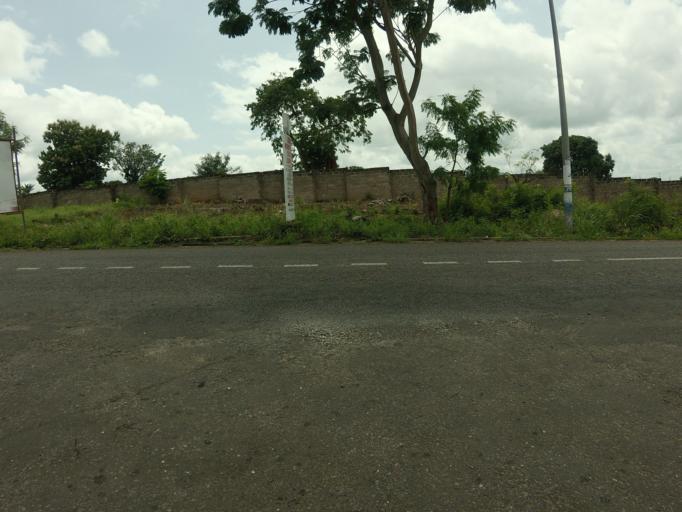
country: GH
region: Volta
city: Ho
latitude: 6.5945
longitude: 0.4776
